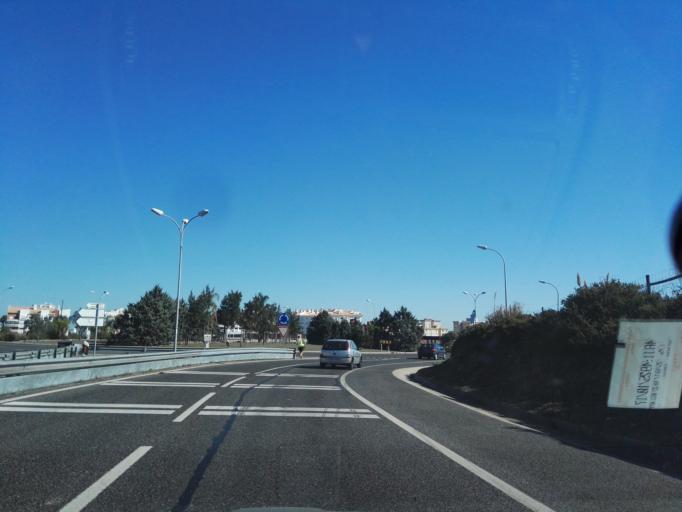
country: PT
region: Lisbon
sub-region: Sintra
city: Sintra
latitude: 38.8032
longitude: -9.3582
